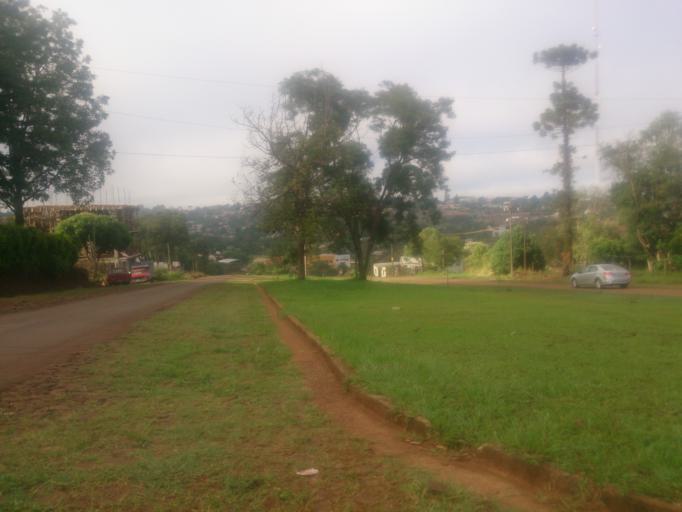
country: AR
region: Misiones
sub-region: Departamento de Obera
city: Obera
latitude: -27.4762
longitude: -55.1064
